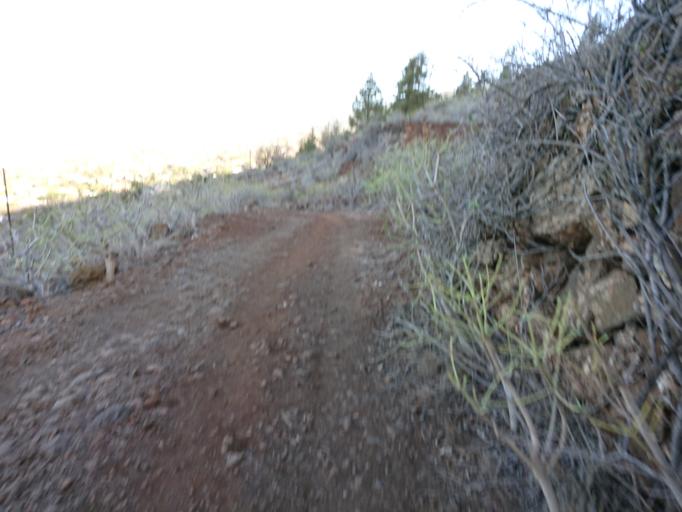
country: ES
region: Canary Islands
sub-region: Provincia de Santa Cruz de Tenerife
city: Los Llanos de Aridane
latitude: 28.6715
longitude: -17.9414
